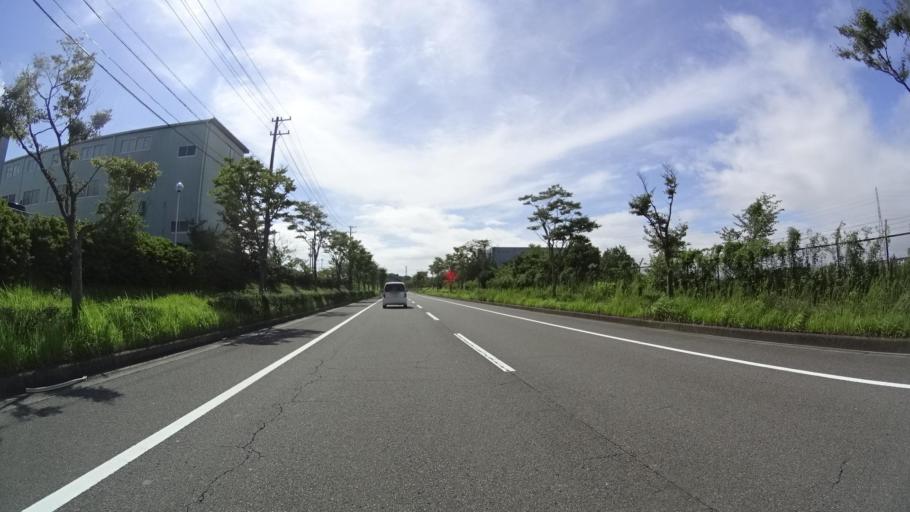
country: JP
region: Mie
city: Kawage
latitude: 34.8369
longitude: 136.5363
